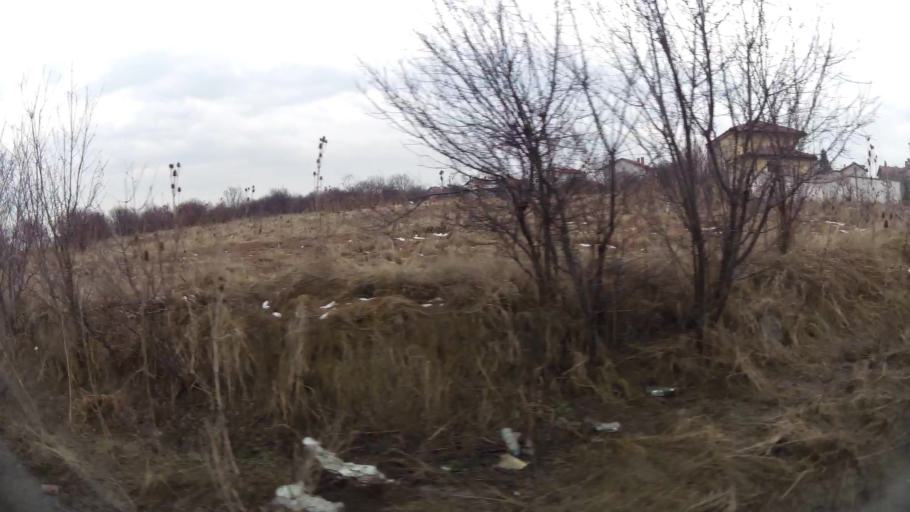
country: BG
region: Sofiya
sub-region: Obshtina Bozhurishte
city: Bozhurishte
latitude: 42.6994
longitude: 23.2194
